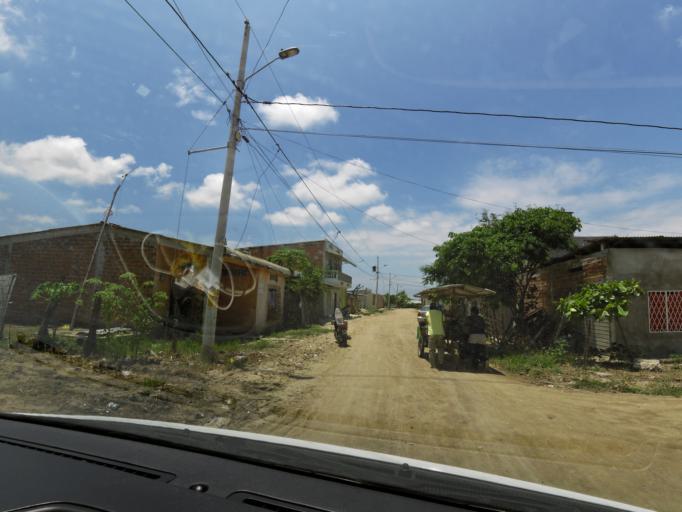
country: EC
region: El Oro
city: Huaquillas
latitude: -3.4693
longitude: -80.2348
